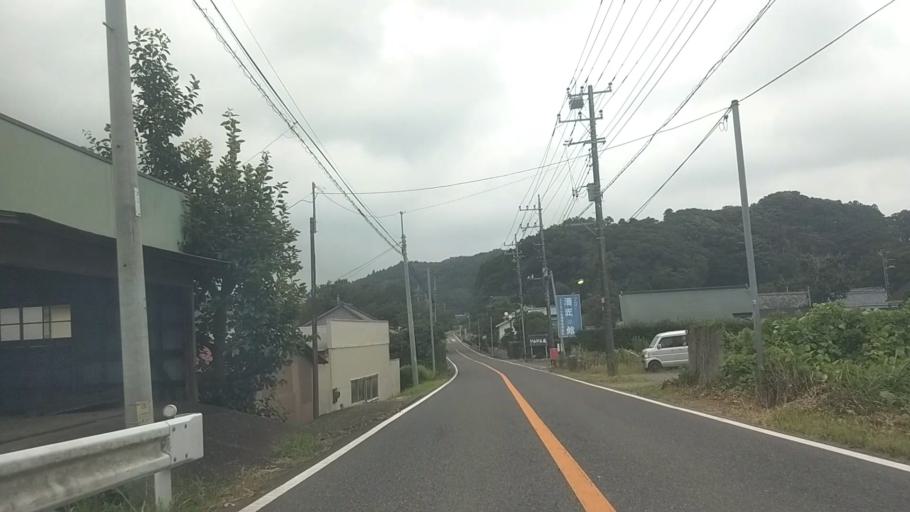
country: JP
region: Chiba
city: Kimitsu
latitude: 35.2172
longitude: 139.9310
